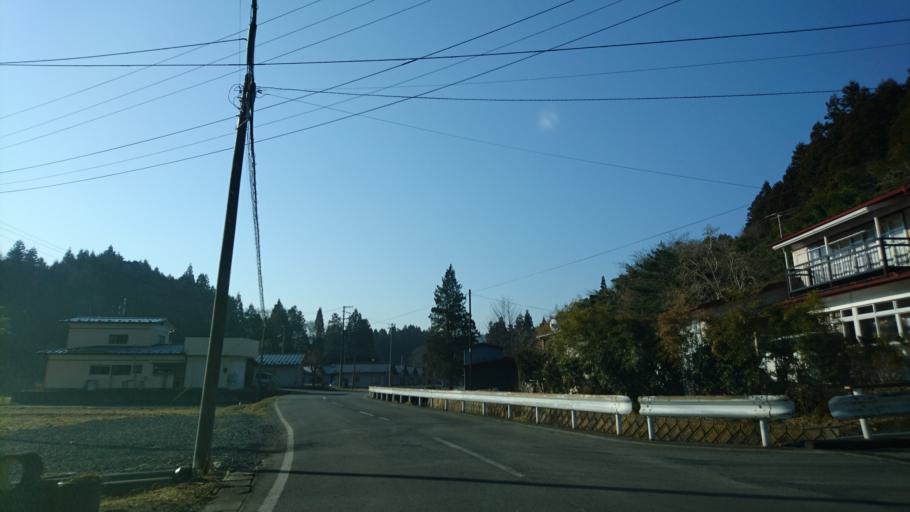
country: JP
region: Iwate
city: Ichinoseki
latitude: 38.9062
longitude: 141.2799
